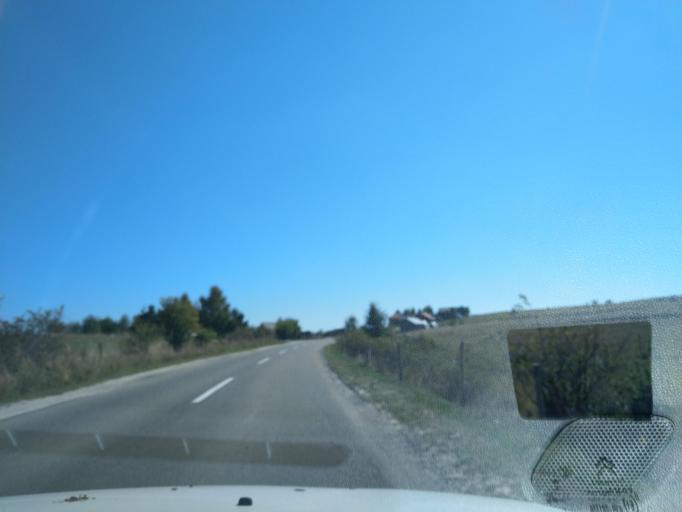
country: RS
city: Sokolovica
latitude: 43.2751
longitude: 20.2220
